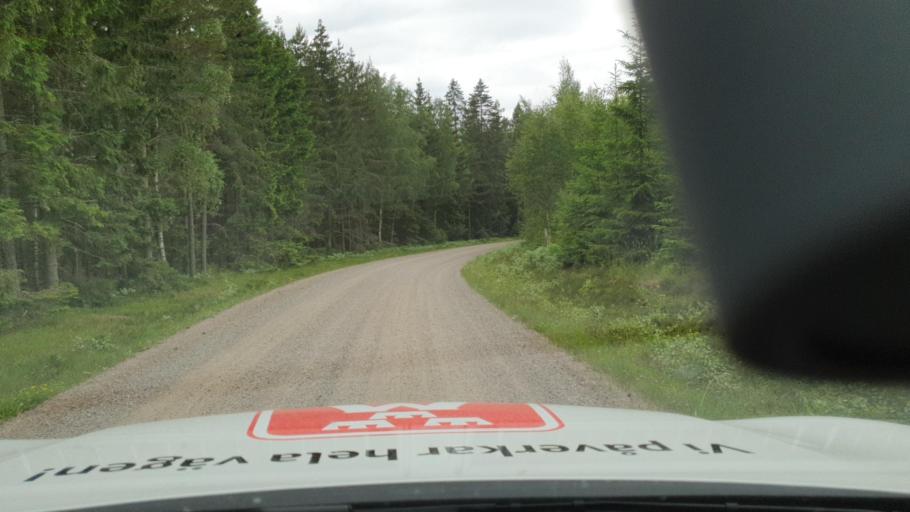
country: SE
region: Vaestra Goetaland
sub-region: Tidaholms Kommun
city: Tidaholm
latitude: 58.1601
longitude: 14.0478
